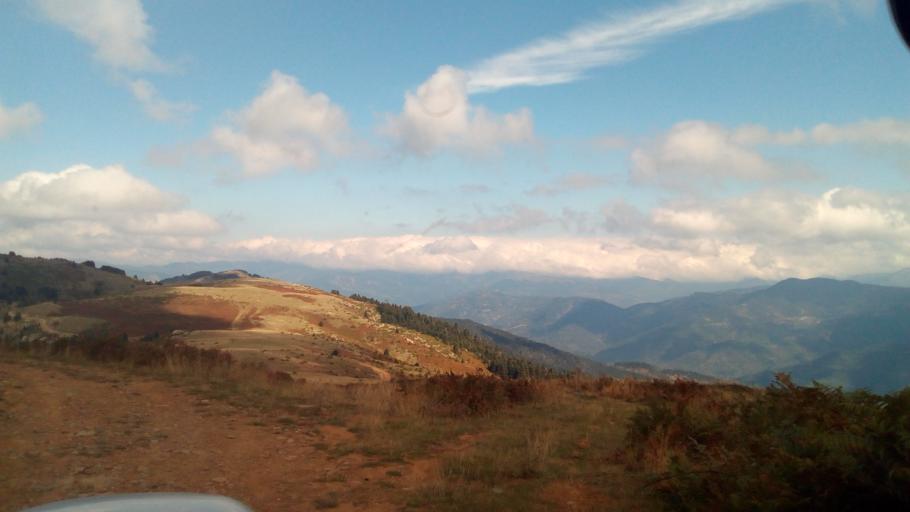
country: GR
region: Central Greece
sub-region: Nomos Fokidos
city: Lidoriki
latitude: 38.6044
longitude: 21.9679
